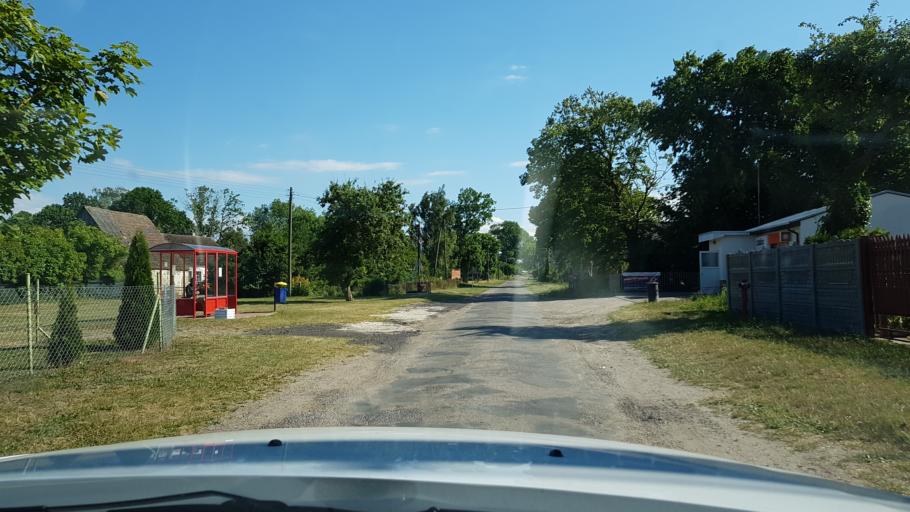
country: PL
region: West Pomeranian Voivodeship
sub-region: Powiat gryficki
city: Mrzezyno
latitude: 54.1198
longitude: 15.3166
